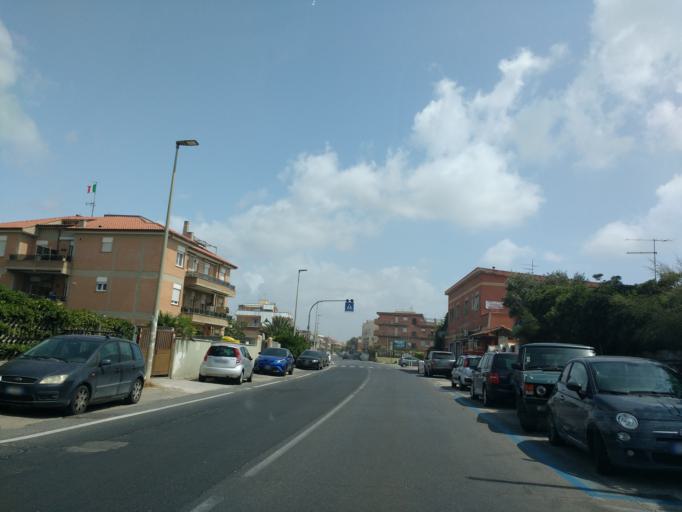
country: IT
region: Latium
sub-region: Citta metropolitana di Roma Capitale
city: Torvaianica
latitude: 41.6335
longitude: 12.4471
